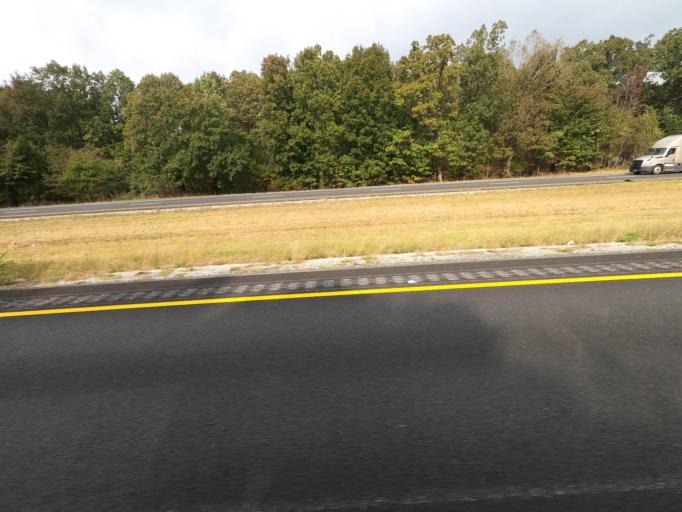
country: US
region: Tennessee
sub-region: Humphreys County
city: McEwen
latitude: 35.9604
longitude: -87.5494
